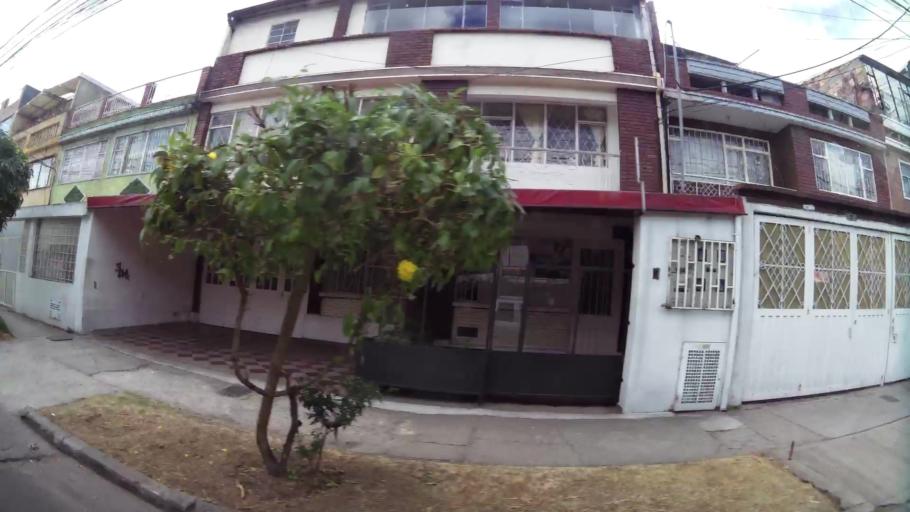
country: CO
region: Bogota D.C.
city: Bogota
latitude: 4.5967
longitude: -74.1238
